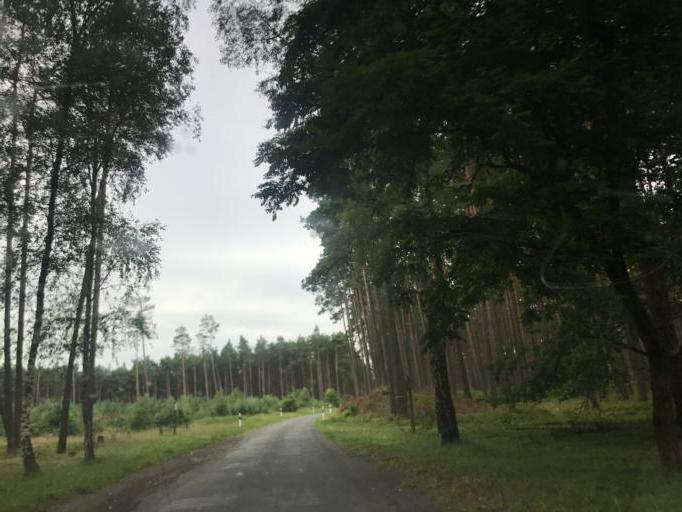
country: DE
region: Mecklenburg-Vorpommern
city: Wesenberg
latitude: 53.2884
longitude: 12.8879
